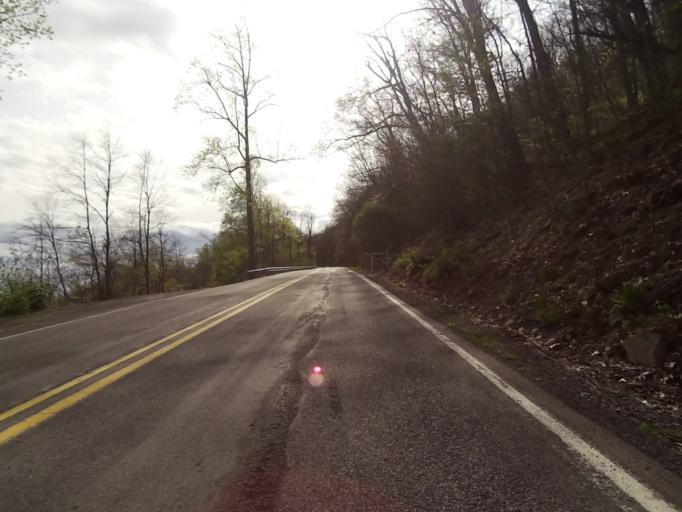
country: US
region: Pennsylvania
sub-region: Centre County
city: Stormstown
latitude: 40.8843
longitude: -77.9987
